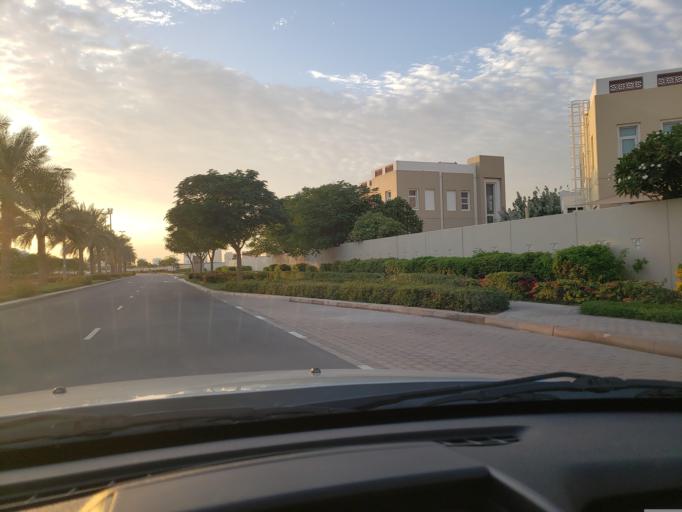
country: AE
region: Dubai
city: Dubai
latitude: 25.0198
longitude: 55.2720
